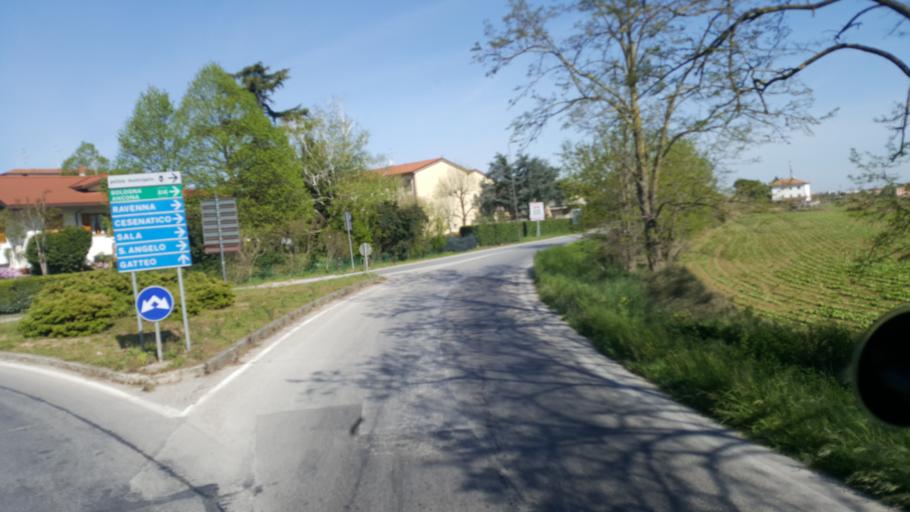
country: IT
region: Emilia-Romagna
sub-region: Forli-Cesena
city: Gatteo-Sant'Angelo
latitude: 44.1052
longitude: 12.3894
